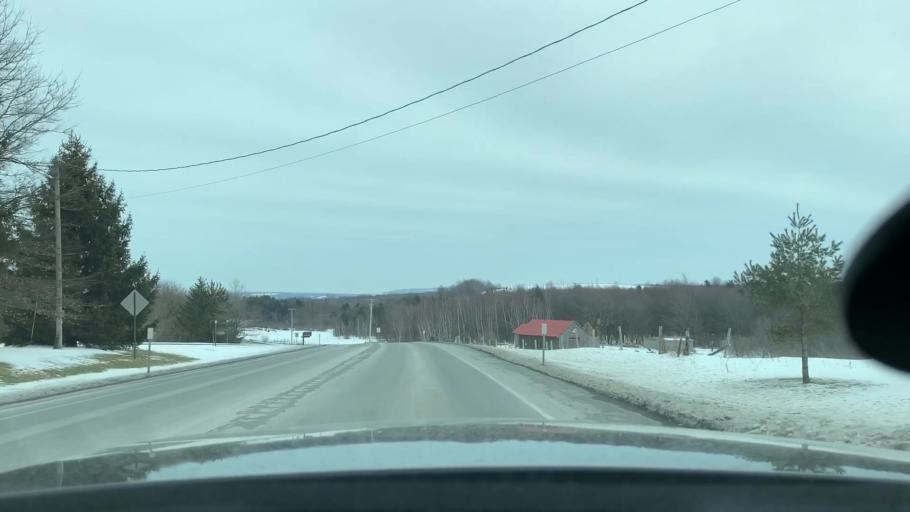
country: US
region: New York
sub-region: Oneida County
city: Utica
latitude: 43.0307
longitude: -75.1722
